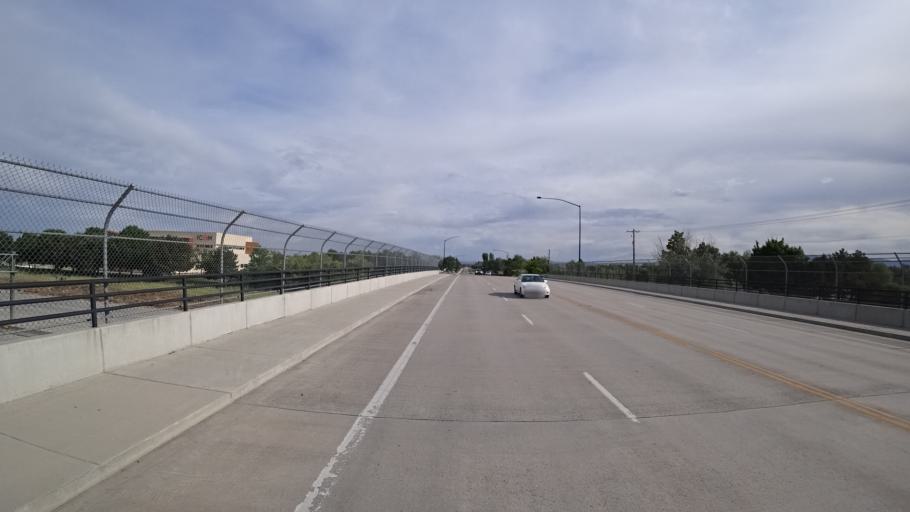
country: US
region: Idaho
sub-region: Ada County
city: Meridian
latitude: 43.5932
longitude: -116.3746
